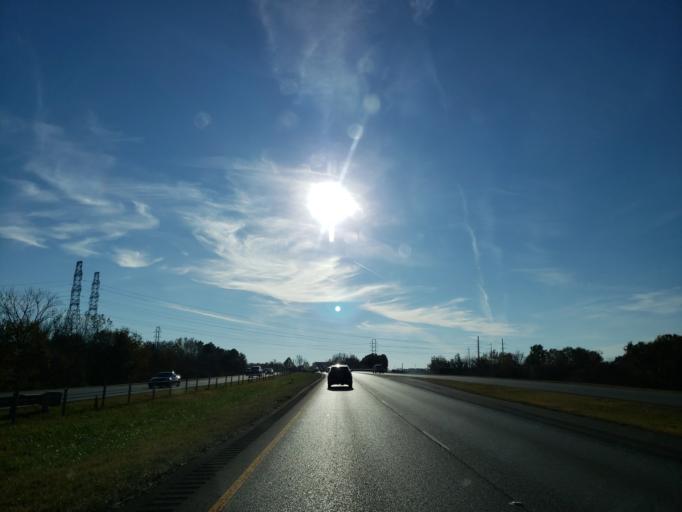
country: US
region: Alabama
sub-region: Jefferson County
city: Brighton
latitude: 33.4243
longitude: -86.9576
